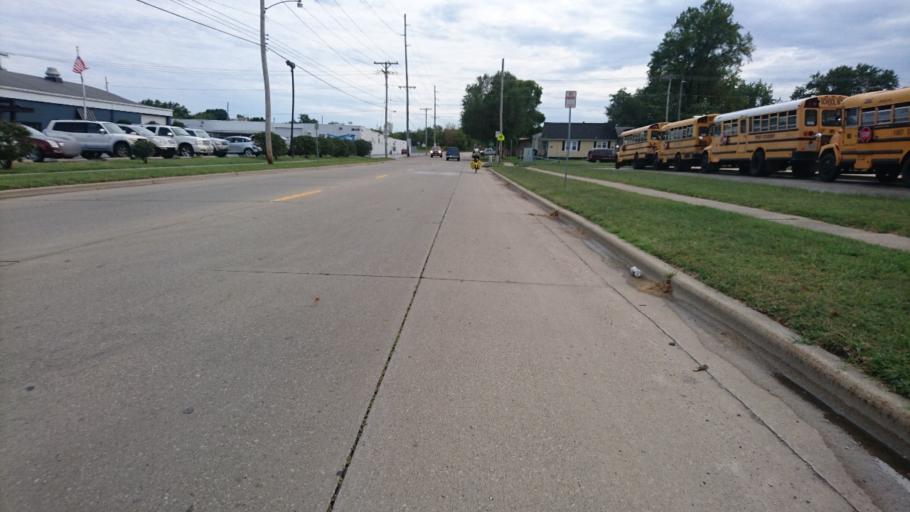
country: US
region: Illinois
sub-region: Sangamon County
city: Southern View
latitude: 39.7726
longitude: -89.6543
